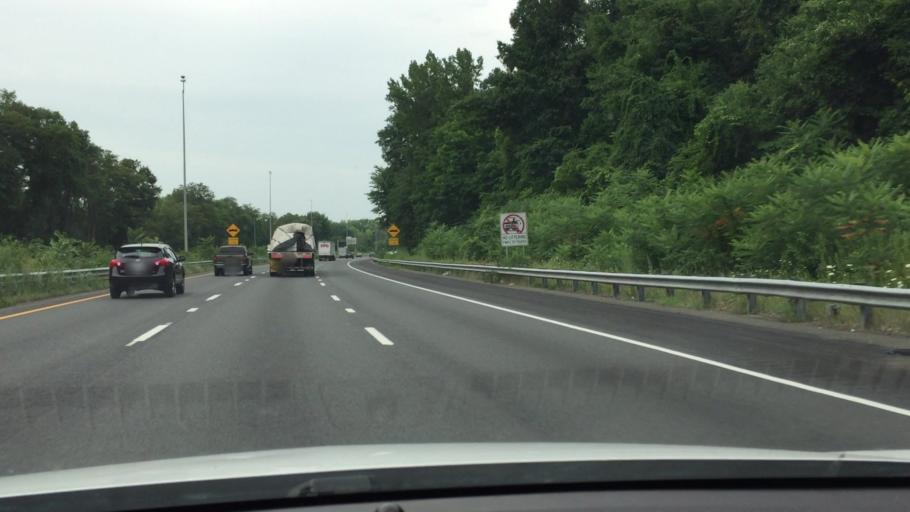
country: US
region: Massachusetts
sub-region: Hampden County
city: Longmeadow
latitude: 42.0266
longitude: -72.5901
